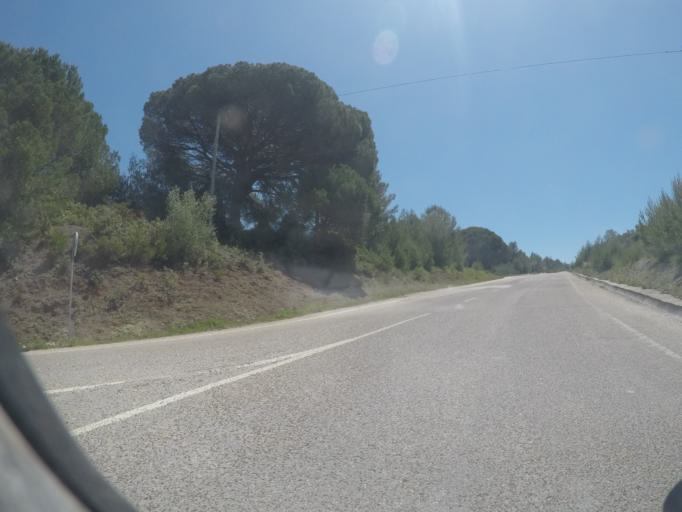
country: PT
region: Setubal
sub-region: Sesimbra
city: Sesimbra
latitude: 38.4642
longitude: -9.0793
